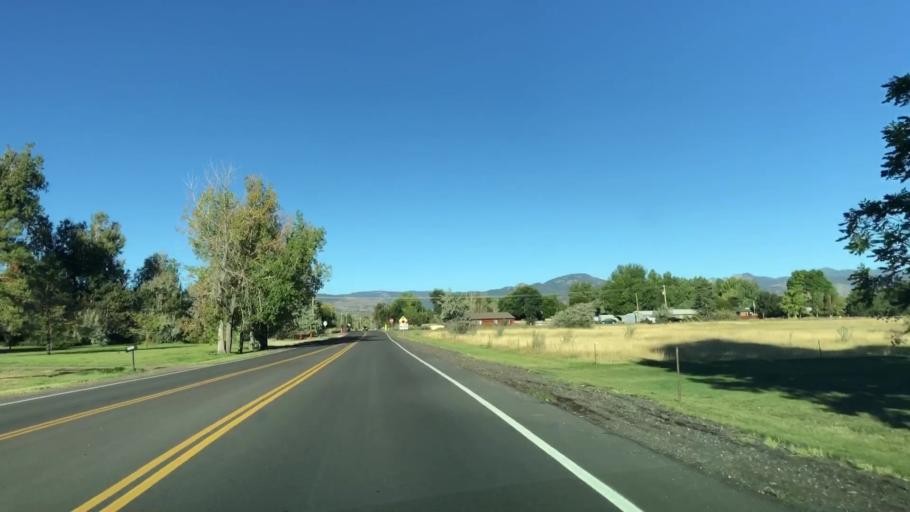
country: US
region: Colorado
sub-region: Larimer County
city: Loveland
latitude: 40.3784
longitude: -105.1324
